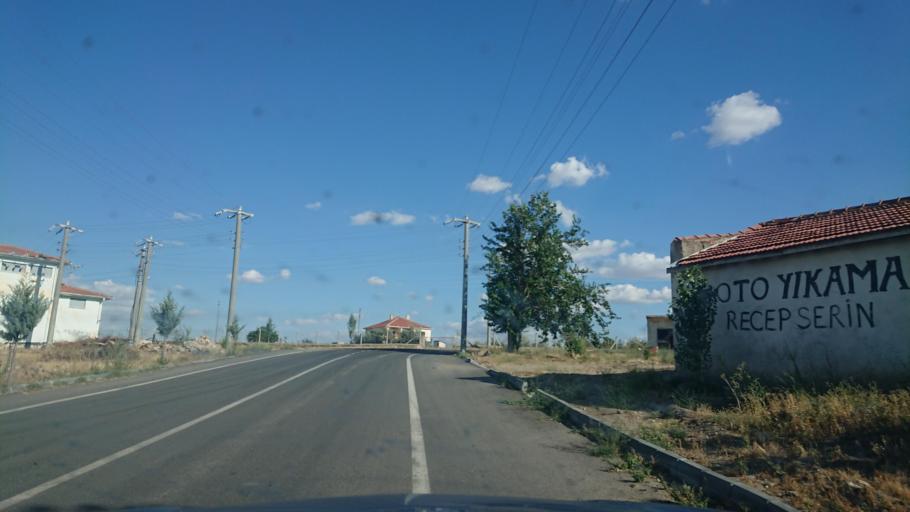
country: TR
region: Aksaray
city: Sariyahsi
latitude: 38.9863
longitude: 33.8529
